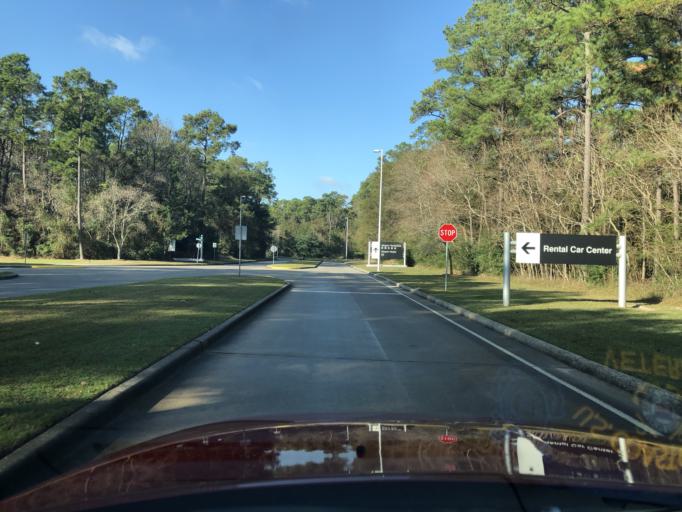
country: US
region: Texas
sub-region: Harris County
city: Aldine
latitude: 29.9727
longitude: -95.3349
